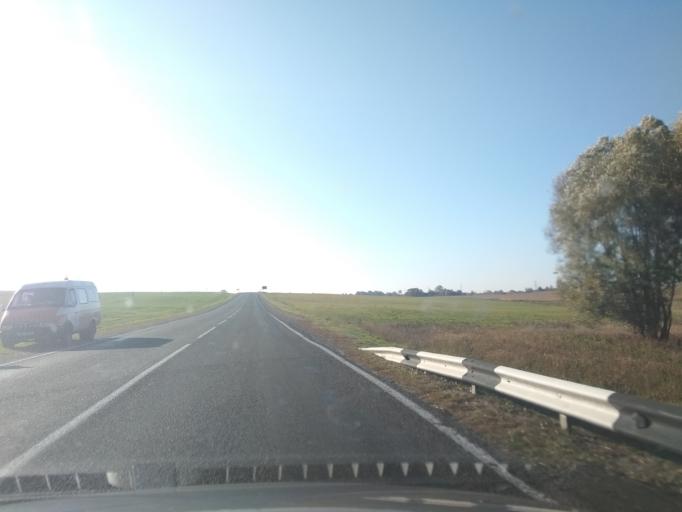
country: BY
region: Grodnenskaya
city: Svislach
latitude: 53.1337
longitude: 24.2249
